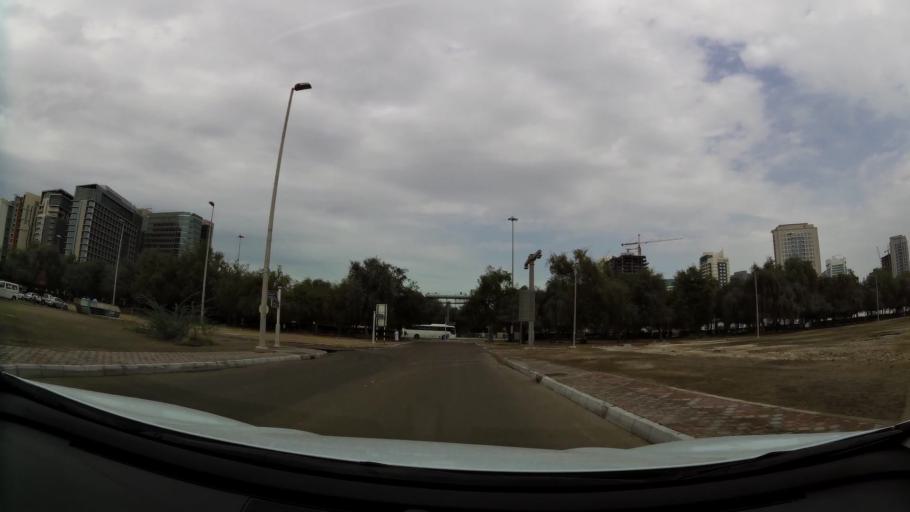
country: AE
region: Abu Dhabi
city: Abu Dhabi
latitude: 24.4273
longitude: 54.4307
